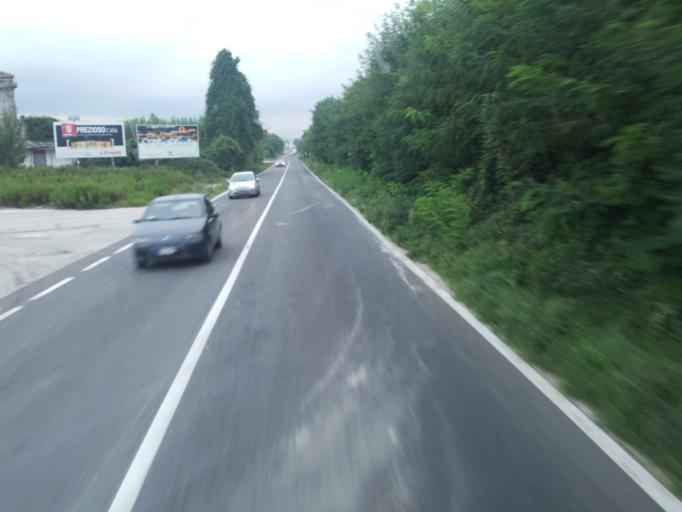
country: IT
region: Campania
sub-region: Provincia di Caserta
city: Pignataro Maggiore
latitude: 41.1685
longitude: 14.1497
